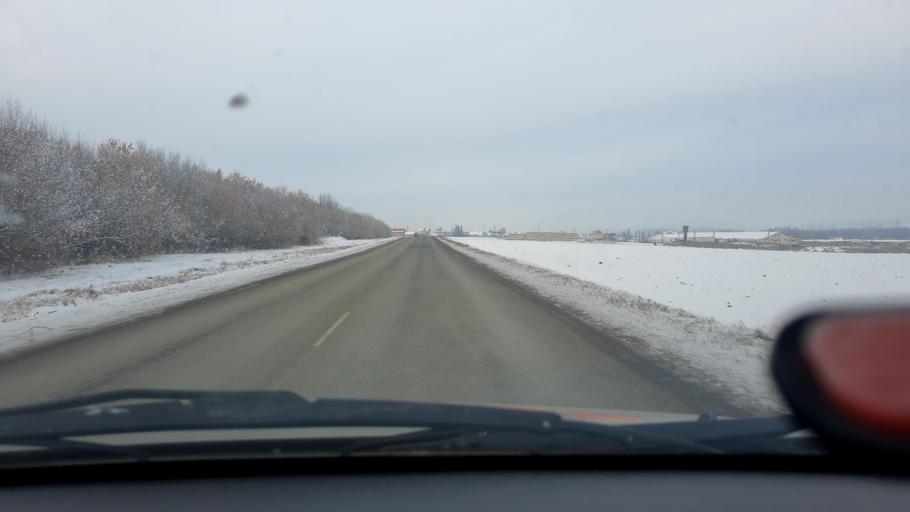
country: RU
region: Bashkortostan
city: Avdon
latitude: 54.4053
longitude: 55.8056
